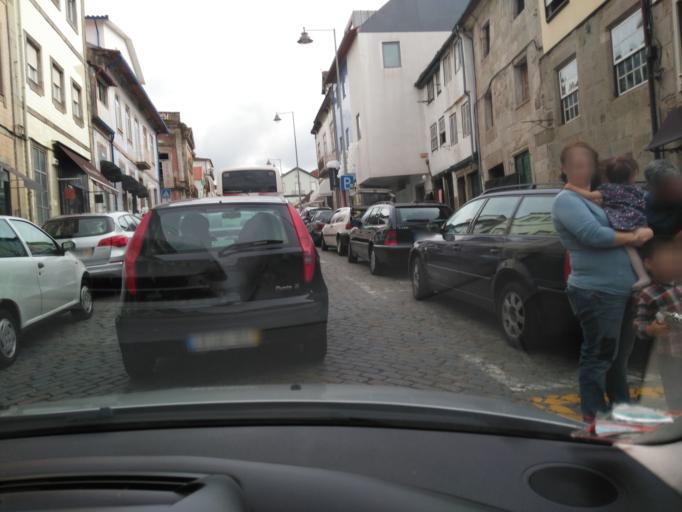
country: PT
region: Braga
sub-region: Braga
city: Braga
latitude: 41.5502
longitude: -8.4286
